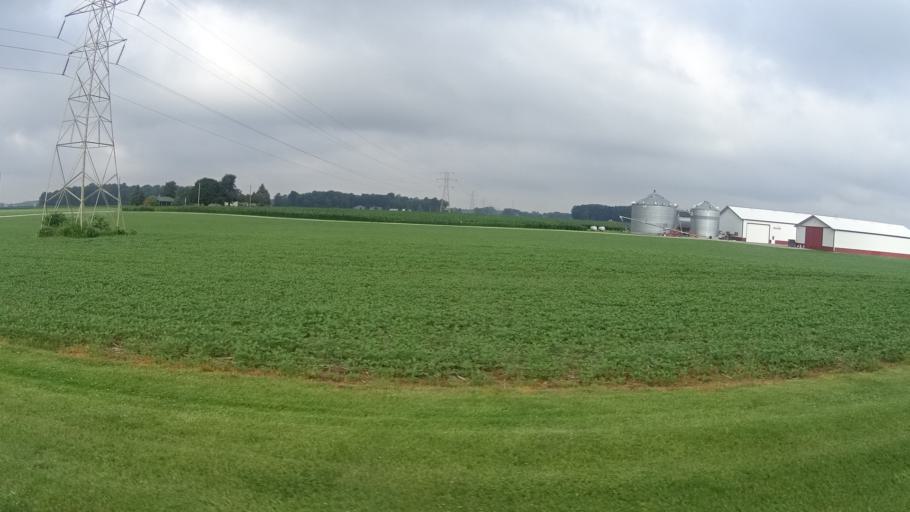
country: US
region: Ohio
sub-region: Erie County
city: Huron
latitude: 41.3587
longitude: -82.5176
